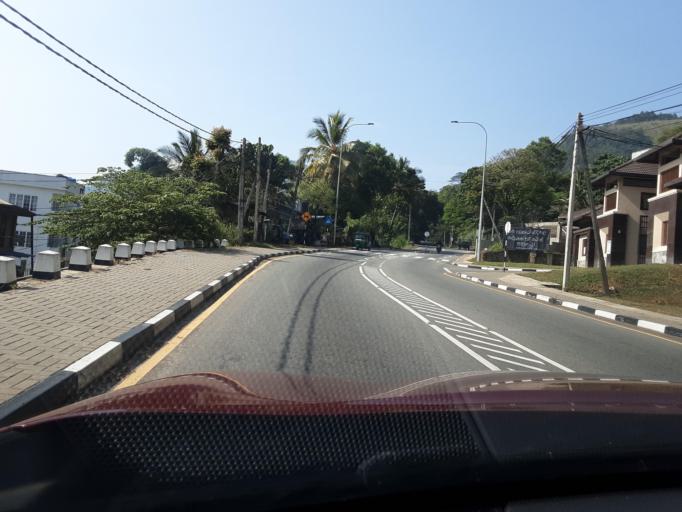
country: LK
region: Uva
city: Badulla
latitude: 6.9836
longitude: 81.0793
